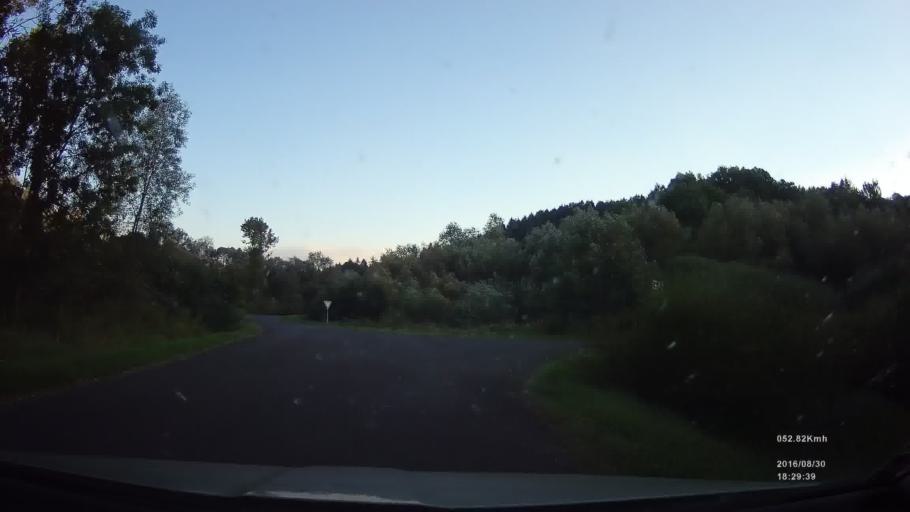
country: SK
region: Zilinsky
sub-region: Okres Liptovsky Mikulas
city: Liptovsky Mikulas
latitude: 49.1308
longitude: 19.5009
